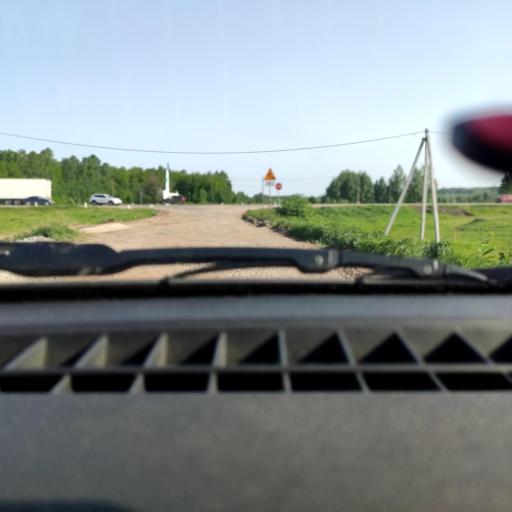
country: RU
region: Bashkortostan
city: Iglino
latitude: 54.7367
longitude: 56.2790
